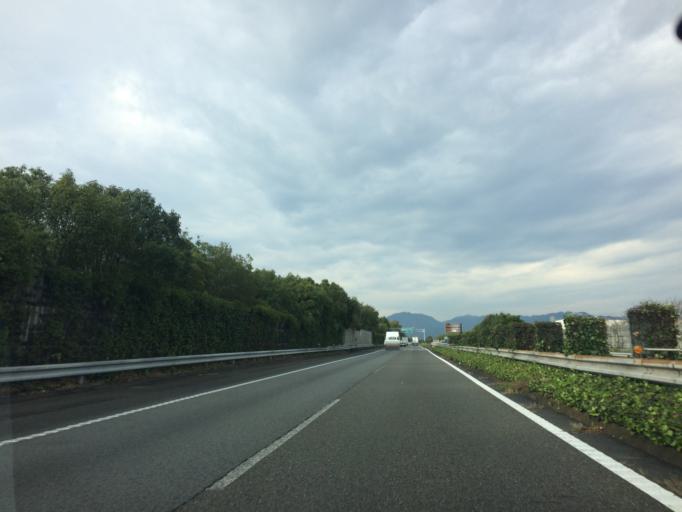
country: JP
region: Shizuoka
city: Shizuoka-shi
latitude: 34.9589
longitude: 138.4182
